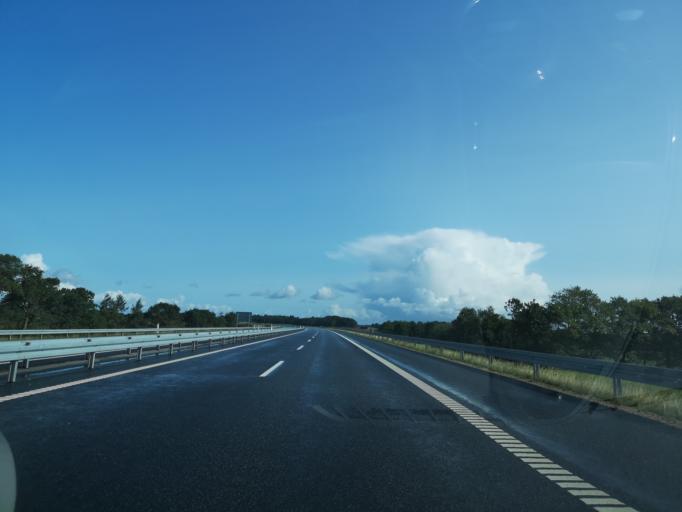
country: DK
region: Central Jutland
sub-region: Herning Kommune
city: Snejbjerg
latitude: 56.1609
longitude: 8.8825
